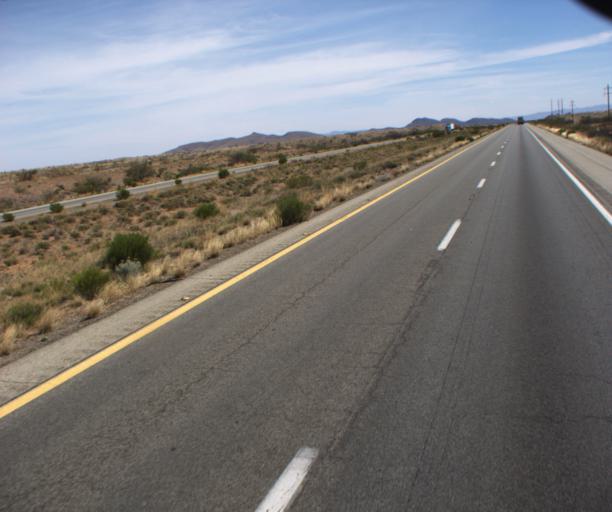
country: US
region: Arizona
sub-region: Cochise County
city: Willcox
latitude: 32.3567
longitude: -109.6962
